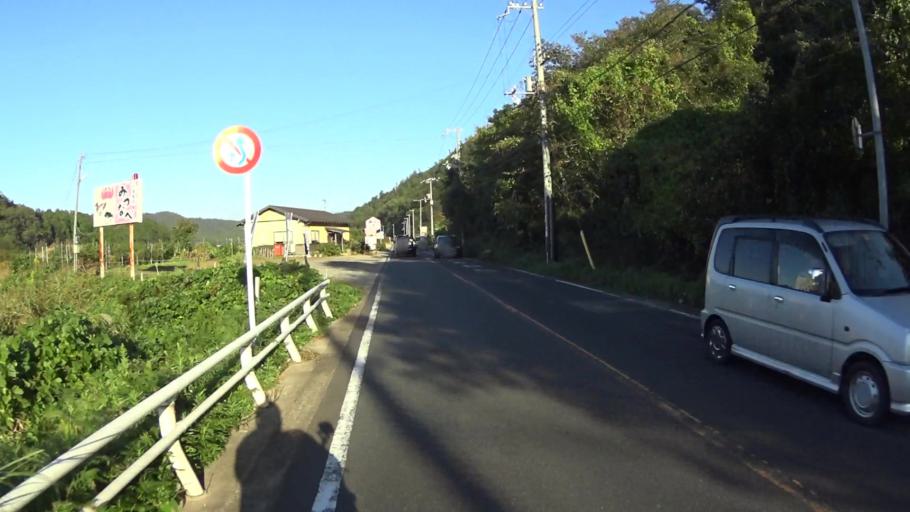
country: JP
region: Hyogo
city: Toyooka
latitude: 35.6050
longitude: 134.9100
